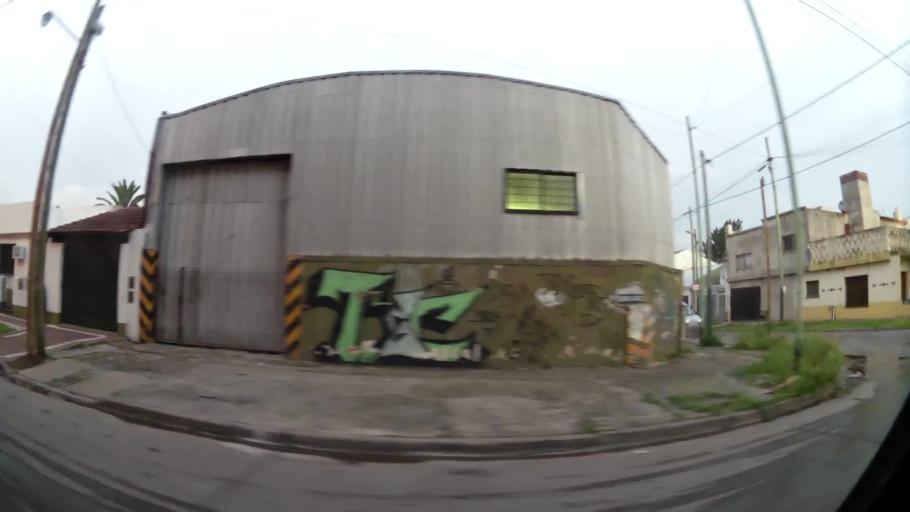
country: AR
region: Buenos Aires
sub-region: Partido de Lomas de Zamora
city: Lomas de Zamora
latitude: -34.7433
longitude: -58.3711
